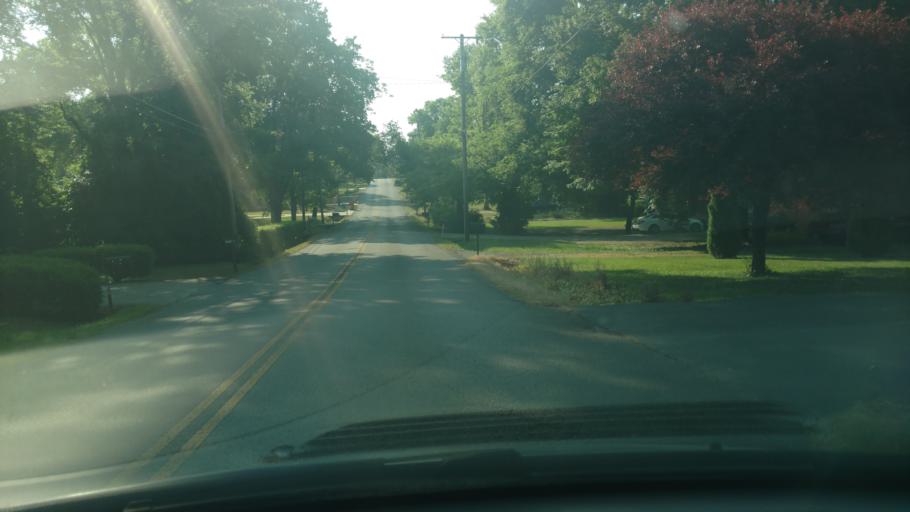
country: US
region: Tennessee
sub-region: Davidson County
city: Nashville
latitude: 36.2221
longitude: -86.7238
